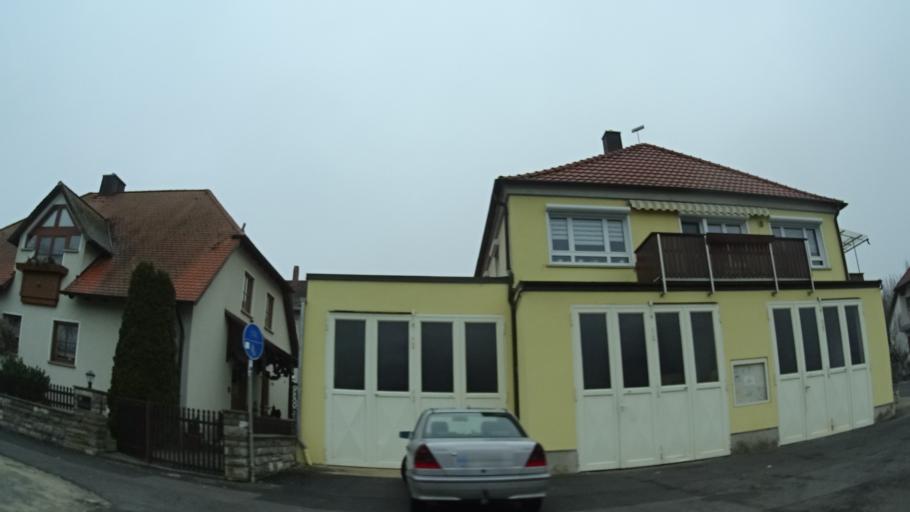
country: DE
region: Bavaria
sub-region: Regierungsbezirk Unterfranken
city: Sulzfeld am Main
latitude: 49.7102
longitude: 10.1359
